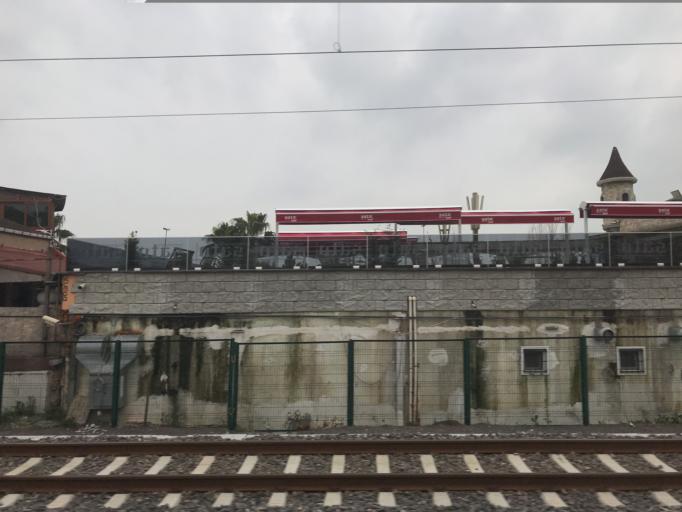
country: TR
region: Istanbul
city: Maltepe
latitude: 40.9394
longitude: 29.1129
